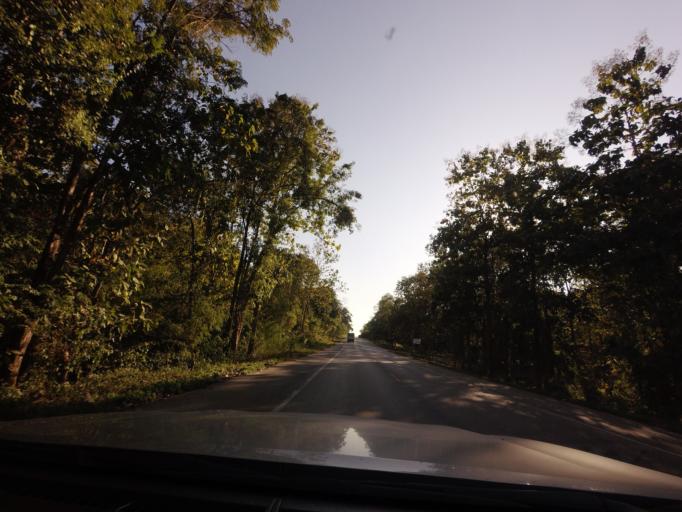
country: TH
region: Lampang
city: Mae Mo
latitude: 18.4947
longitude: 99.6463
